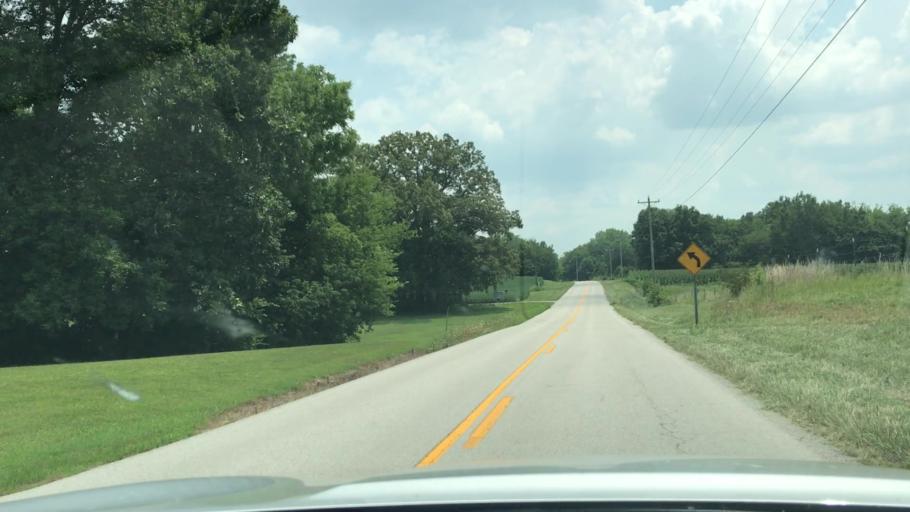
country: US
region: Kentucky
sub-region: Todd County
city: Elkton
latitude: 36.7632
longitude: -87.1065
